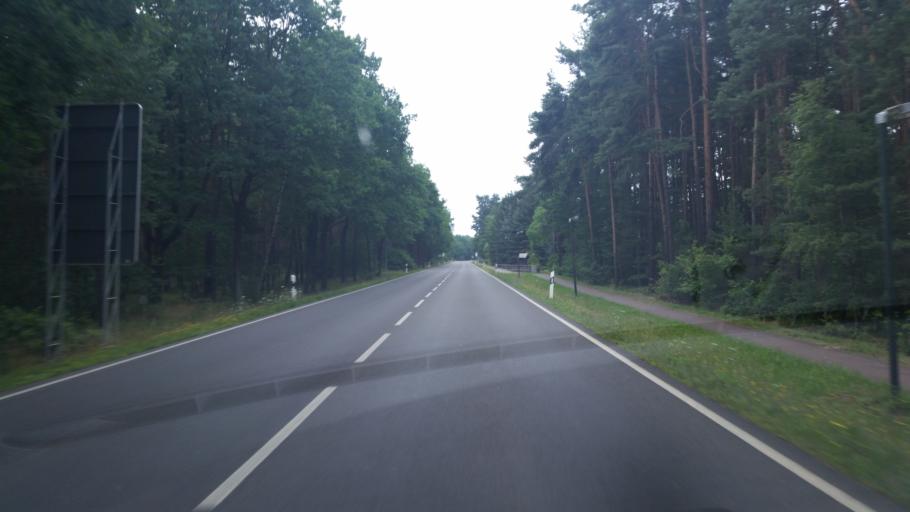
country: DE
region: Brandenburg
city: Senftenberg
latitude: 51.4855
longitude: 14.0681
